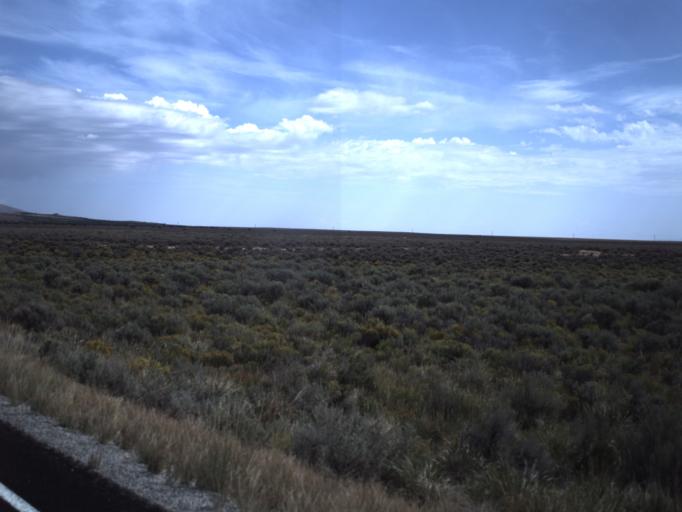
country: US
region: Idaho
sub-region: Cassia County
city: Burley
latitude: 41.7880
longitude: -113.4759
